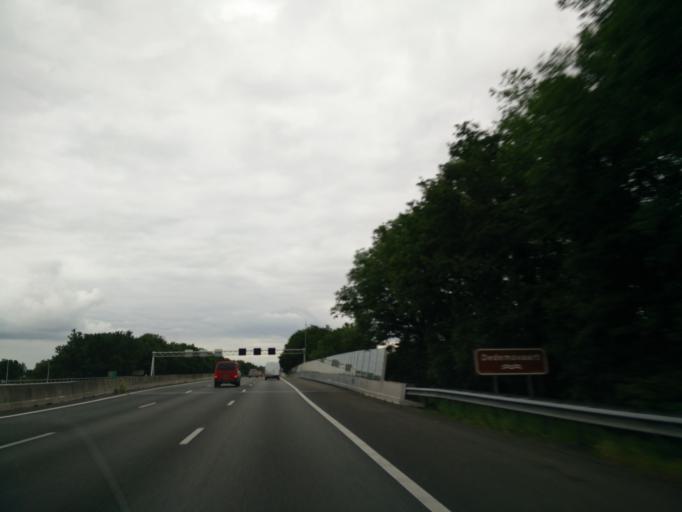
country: NL
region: Overijssel
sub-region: Gemeente Staphorst
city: Staphorst
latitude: 52.5835
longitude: 6.1932
